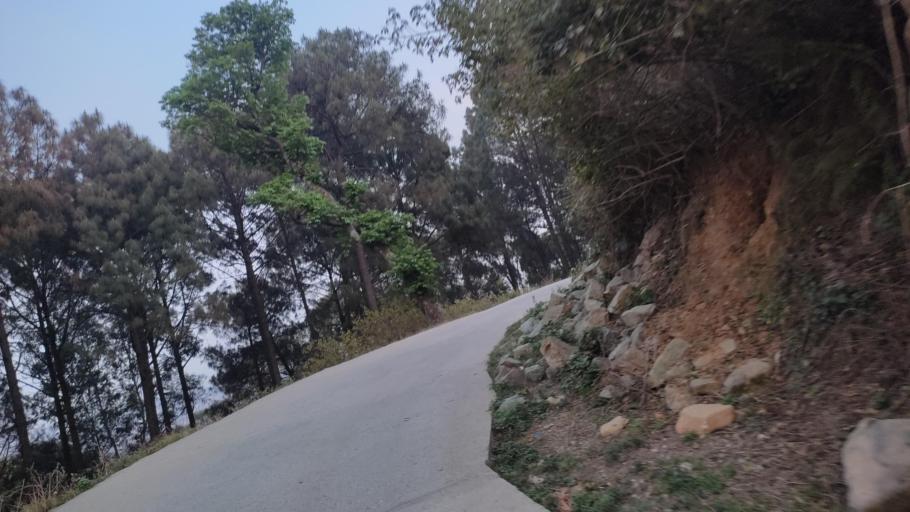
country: NP
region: Central Region
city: Kirtipur
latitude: 27.6671
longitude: 85.2934
